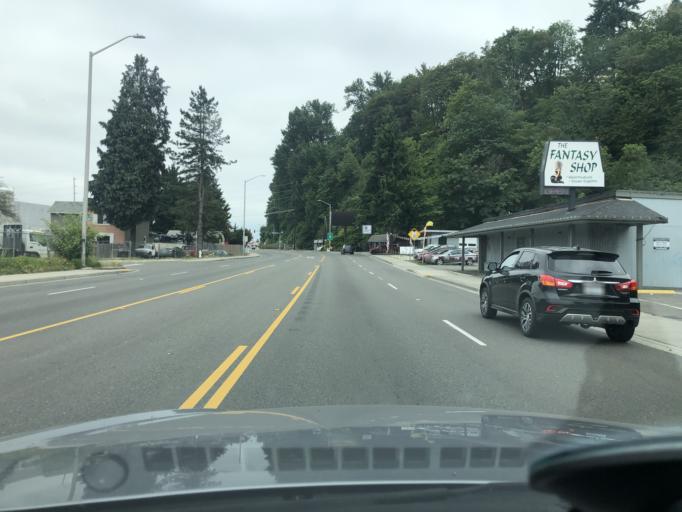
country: US
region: Washington
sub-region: King County
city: Kent
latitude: 47.3761
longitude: -122.2302
